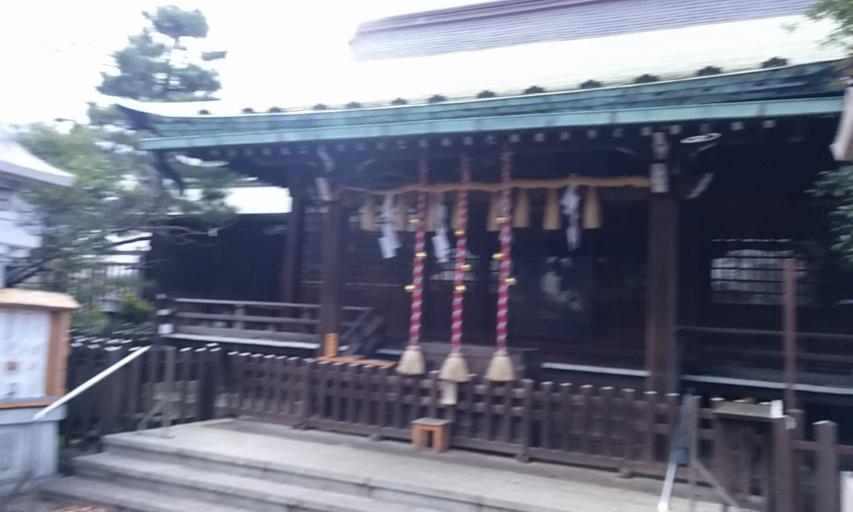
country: JP
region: Tokyo
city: Tokyo
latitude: 35.7168
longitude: 139.6991
